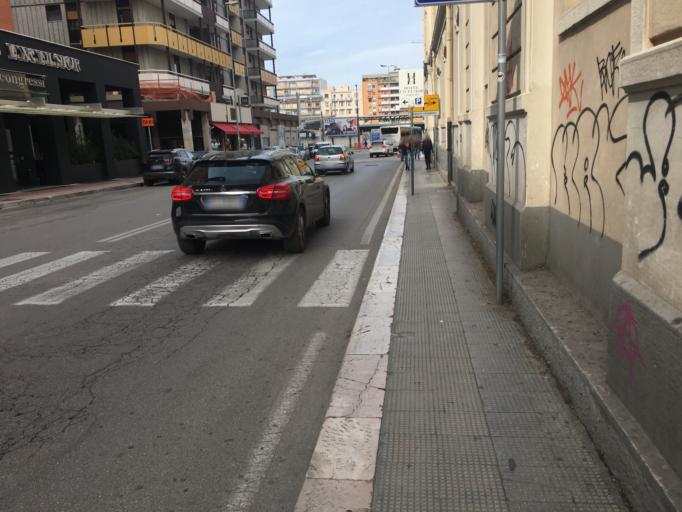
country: IT
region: Apulia
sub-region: Provincia di Bari
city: Bari
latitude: 41.1163
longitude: 16.8689
